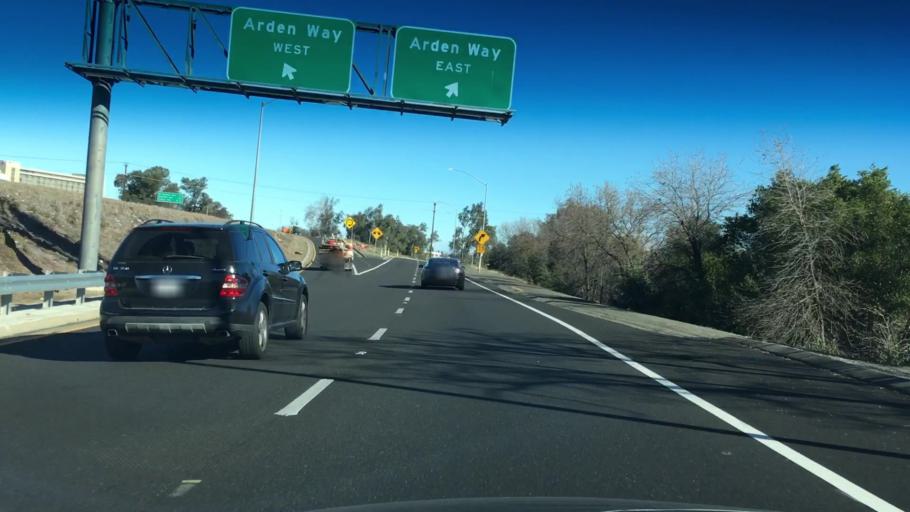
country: US
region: California
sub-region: Sacramento County
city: Arden-Arcade
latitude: 38.6014
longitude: -121.4361
